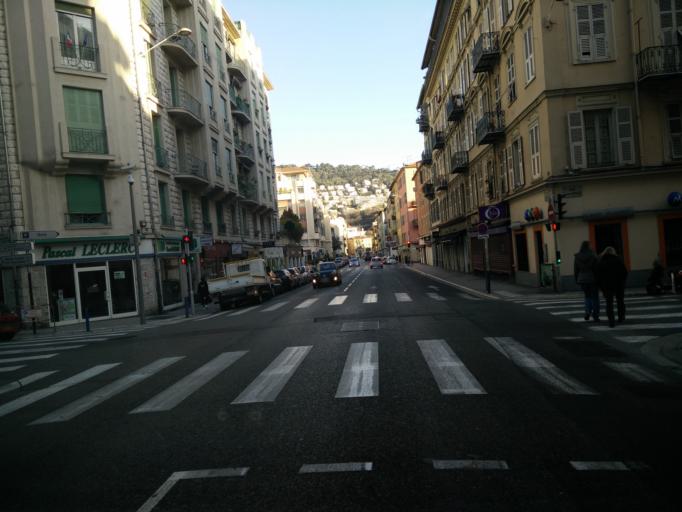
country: FR
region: Provence-Alpes-Cote d'Azur
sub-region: Departement des Alpes-Maritimes
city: Nice
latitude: 43.7017
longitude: 7.2833
